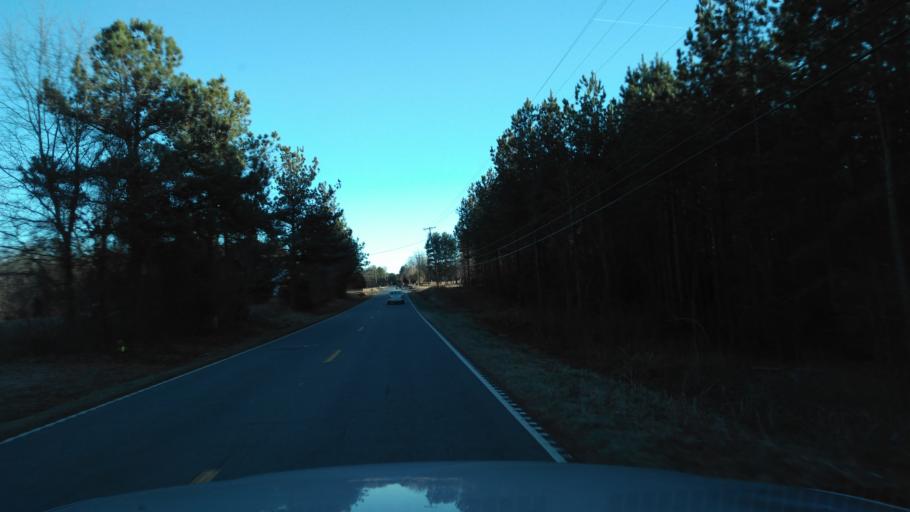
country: US
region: North Carolina
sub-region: Polk County
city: Columbus
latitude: 35.2411
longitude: -82.0863
